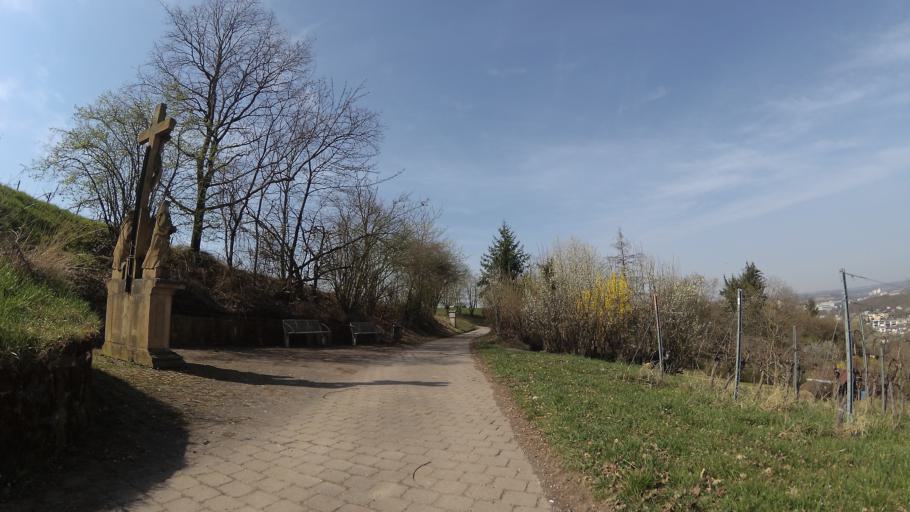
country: DE
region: Baden-Wuerttemberg
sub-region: Regierungsbezirk Stuttgart
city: Neckarsulm
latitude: 49.1969
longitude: 9.2477
